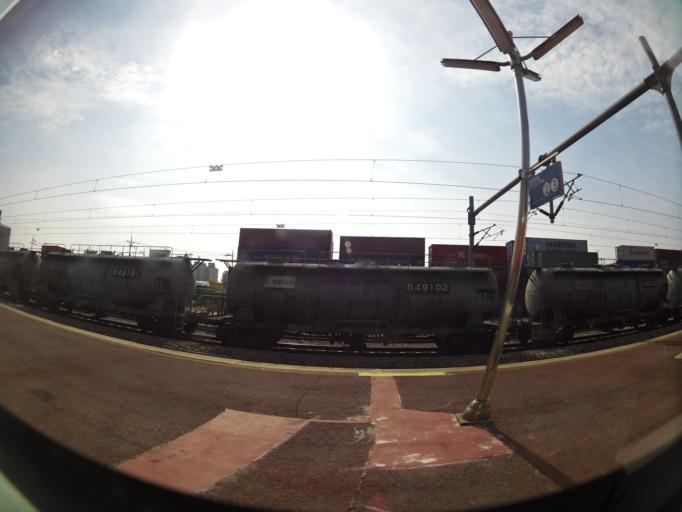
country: KR
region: Daejeon
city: Songgang-dong
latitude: 36.5326
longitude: 127.3642
